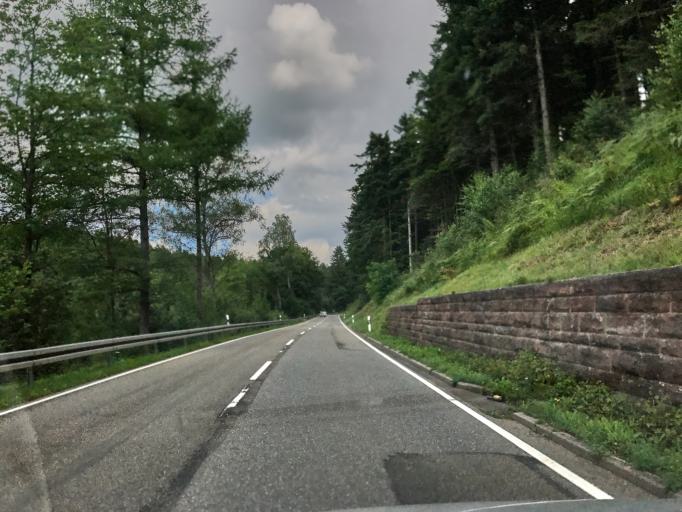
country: DE
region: Baden-Wuerttemberg
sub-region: Karlsruhe Region
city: Lossburg
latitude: 48.4032
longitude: 8.4436
